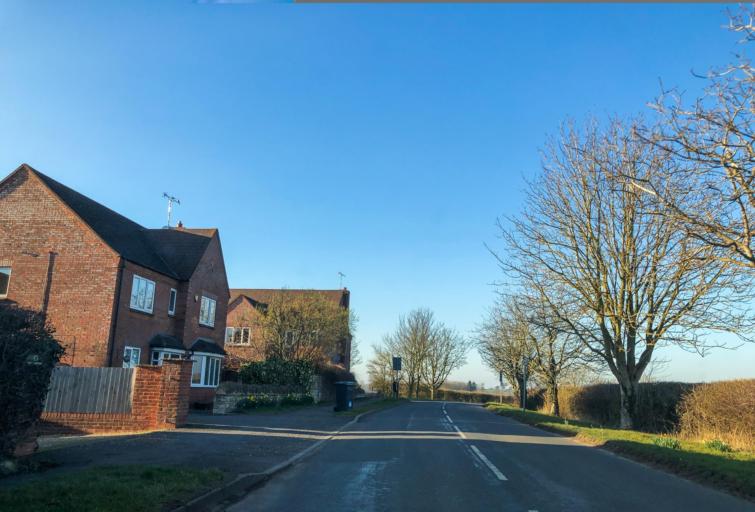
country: GB
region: England
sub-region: Warwickshire
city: Wellesbourne Mountford
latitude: 52.2037
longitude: -1.5472
